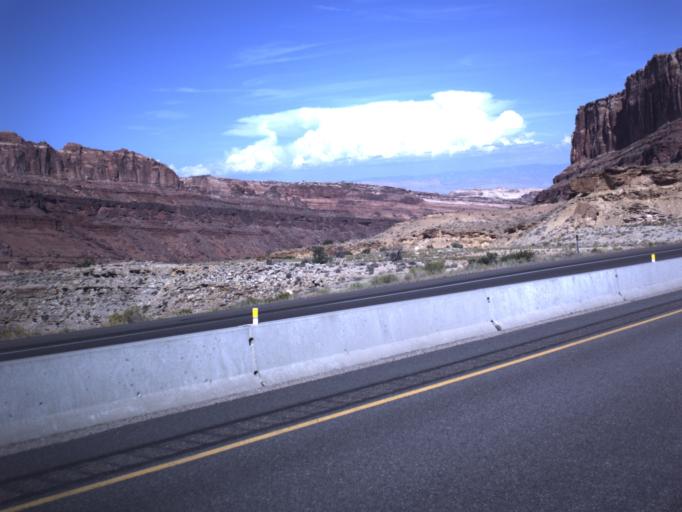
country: US
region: Utah
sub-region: Carbon County
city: East Carbon City
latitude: 38.9375
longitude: -110.4682
